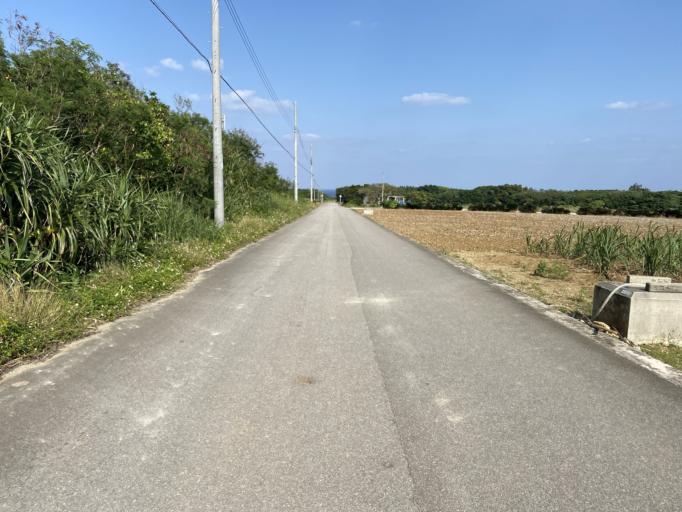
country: JP
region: Okinawa
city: Ishigaki
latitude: 24.0576
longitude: 123.7883
